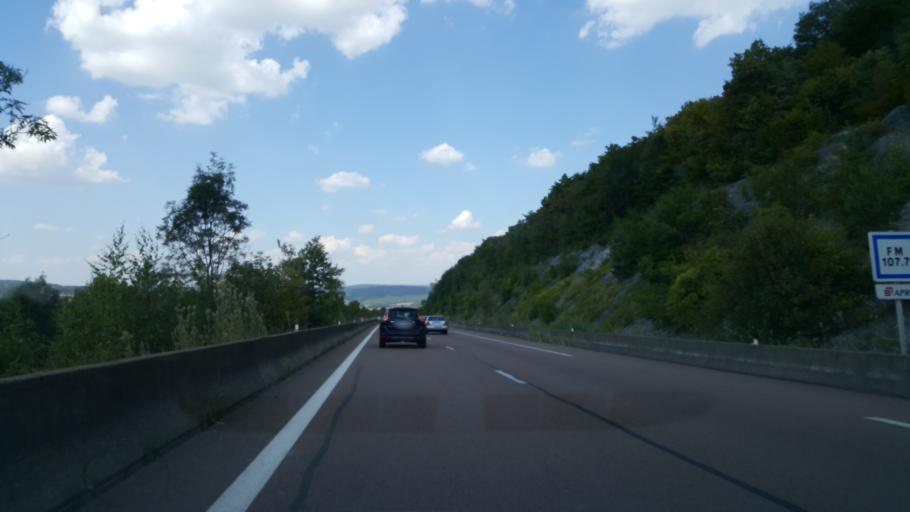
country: FR
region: Bourgogne
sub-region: Departement de la Cote-d'Or
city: Savigny-les-Beaune
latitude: 47.1287
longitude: 4.6994
